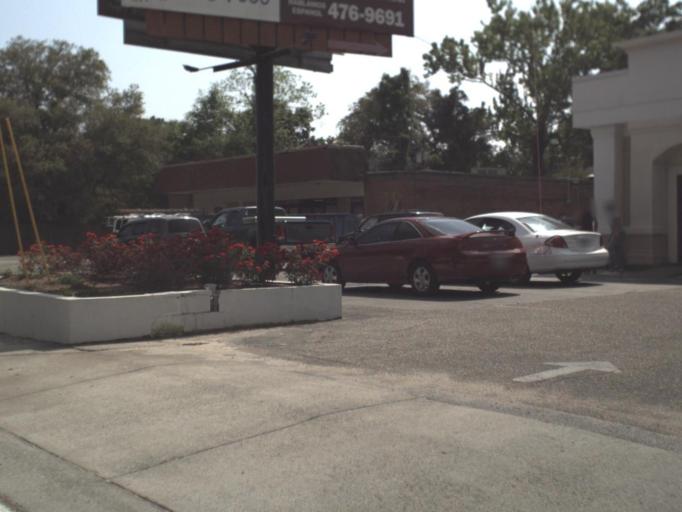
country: US
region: Florida
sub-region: Escambia County
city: Brent
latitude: 30.4684
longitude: -87.2140
